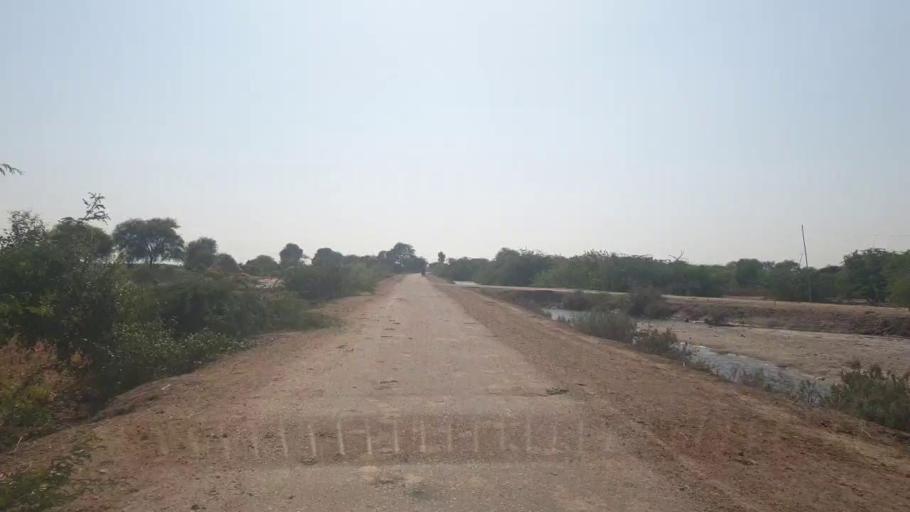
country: PK
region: Sindh
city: Badin
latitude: 24.5523
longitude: 68.8140
